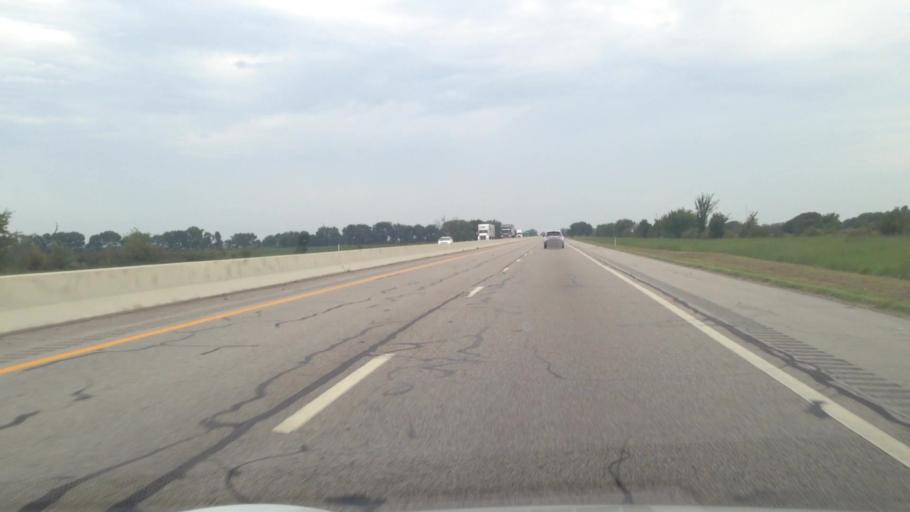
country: US
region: Oklahoma
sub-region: Ottawa County
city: Fairland
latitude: 36.7713
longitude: -94.8942
